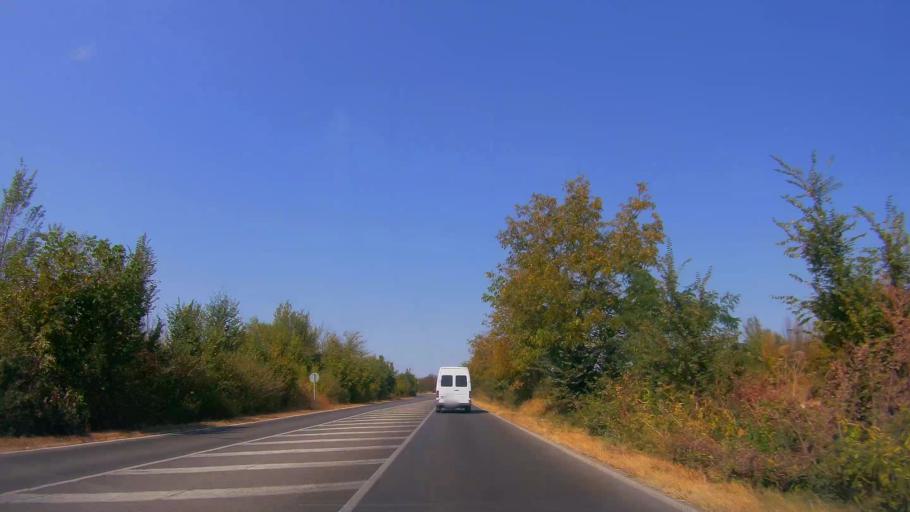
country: BG
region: Razgrad
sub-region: Obshtina Tsar Kaloyan
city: Tsar Kaloyan
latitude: 43.6328
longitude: 26.2013
